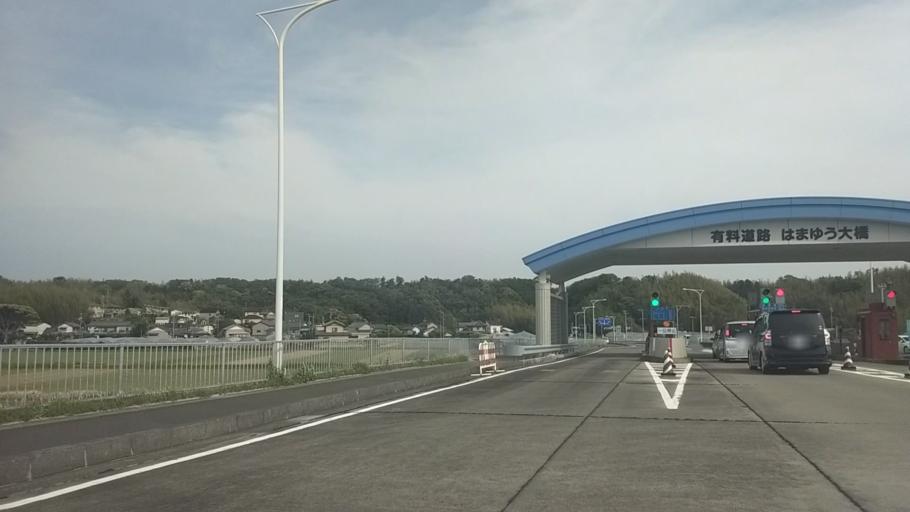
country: JP
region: Shizuoka
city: Kosai-shi
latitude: 34.7267
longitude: 137.6284
